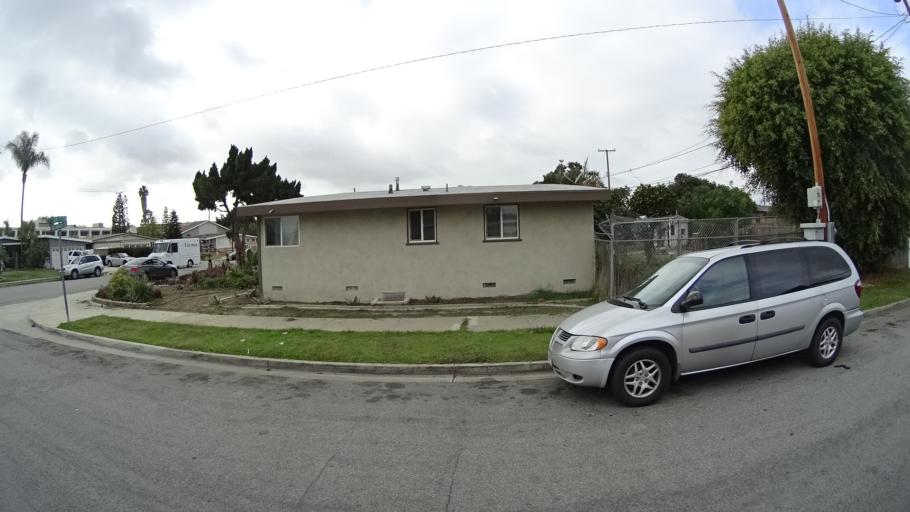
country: US
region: California
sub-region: Orange County
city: Westminster
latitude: 33.7653
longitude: -117.9942
